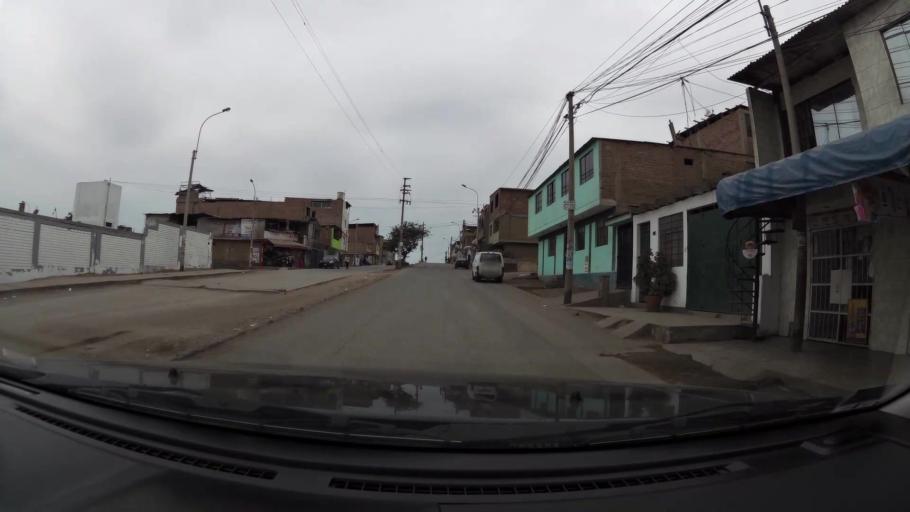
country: PE
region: Lima
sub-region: Lima
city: Surco
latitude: -12.1983
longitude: -76.9465
